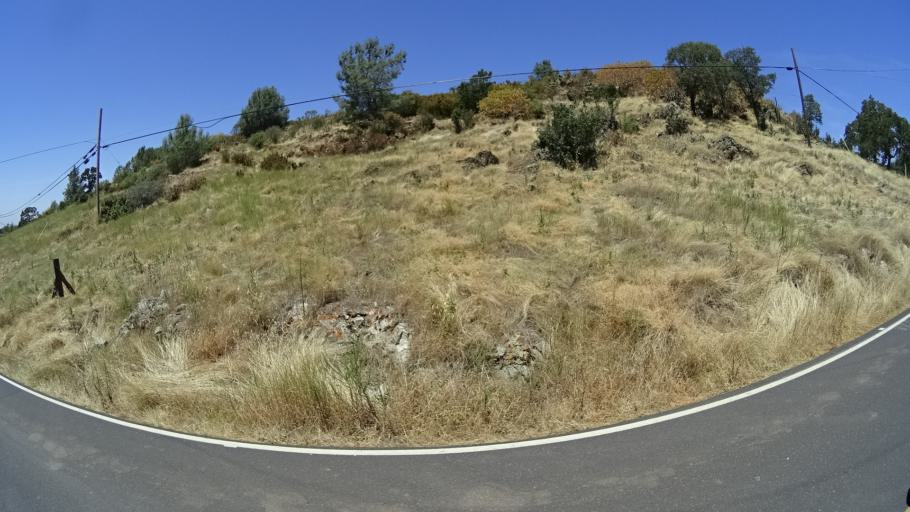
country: US
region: California
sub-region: Calaveras County
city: Valley Springs
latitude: 38.2317
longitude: -120.8000
